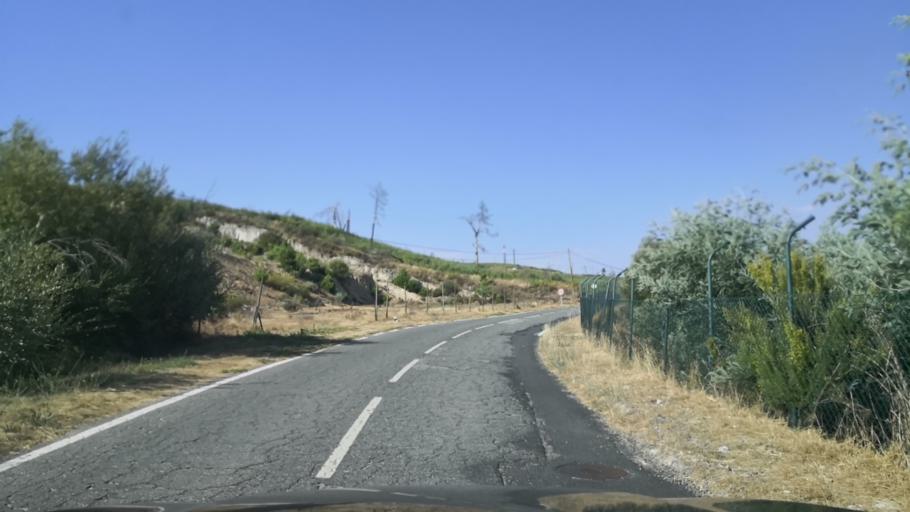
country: PT
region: Vila Real
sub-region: Murca
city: Murca
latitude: 41.3073
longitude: -7.4725
